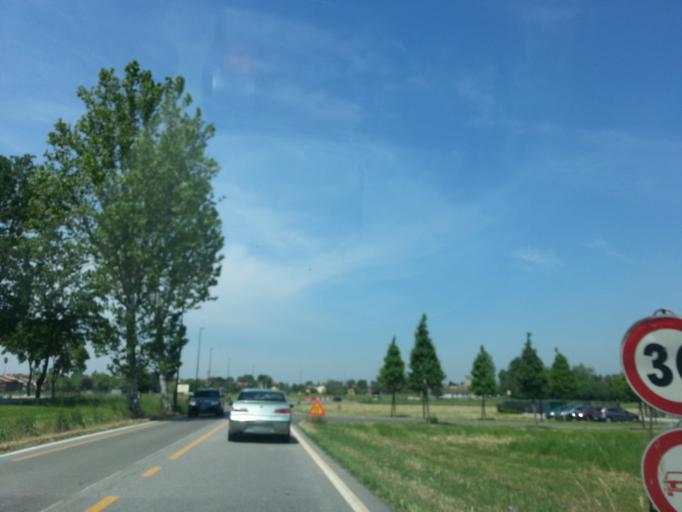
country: IT
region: Emilia-Romagna
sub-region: Provincia di Reggio Emilia
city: Fogliano
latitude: 44.6399
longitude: 10.6536
